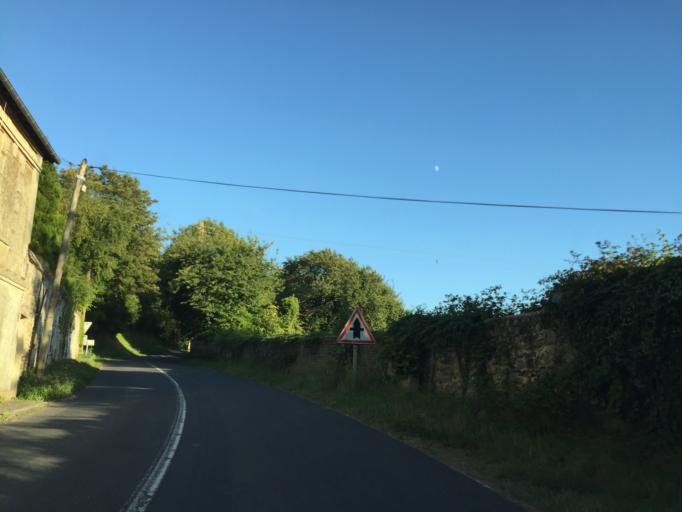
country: FR
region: Lower Normandy
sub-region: Departement du Calvados
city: Equemauville
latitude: 49.4065
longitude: 0.1770
